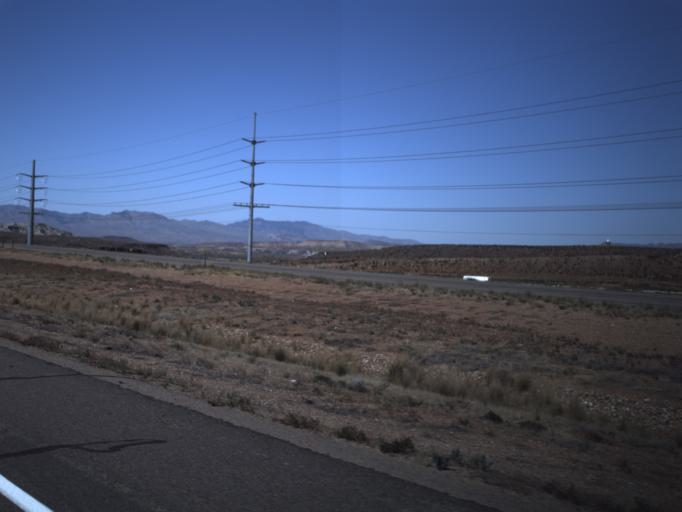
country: US
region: Utah
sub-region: Washington County
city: Saint George
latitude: 37.0097
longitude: -113.5090
